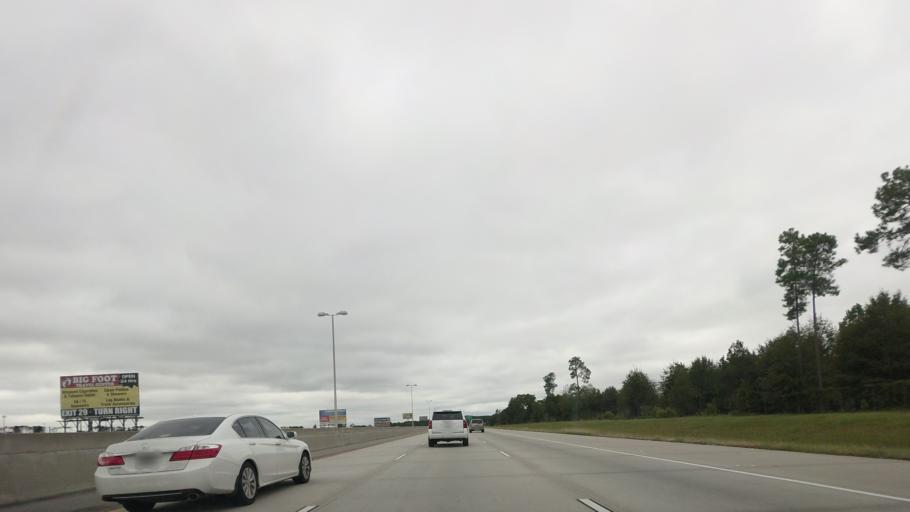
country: US
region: Georgia
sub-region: Cook County
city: Adel
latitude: 31.0649
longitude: -83.4023
